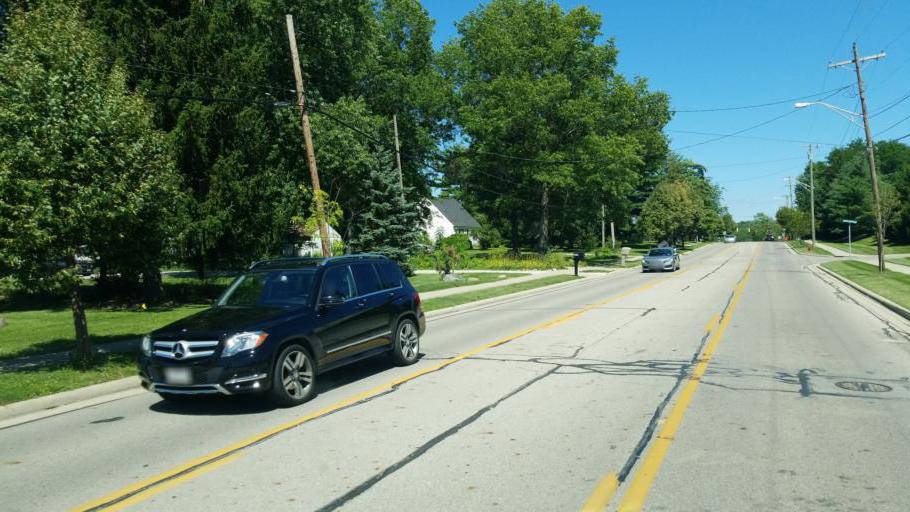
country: US
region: Ohio
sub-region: Franklin County
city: Westerville
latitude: 40.1189
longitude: -82.8888
